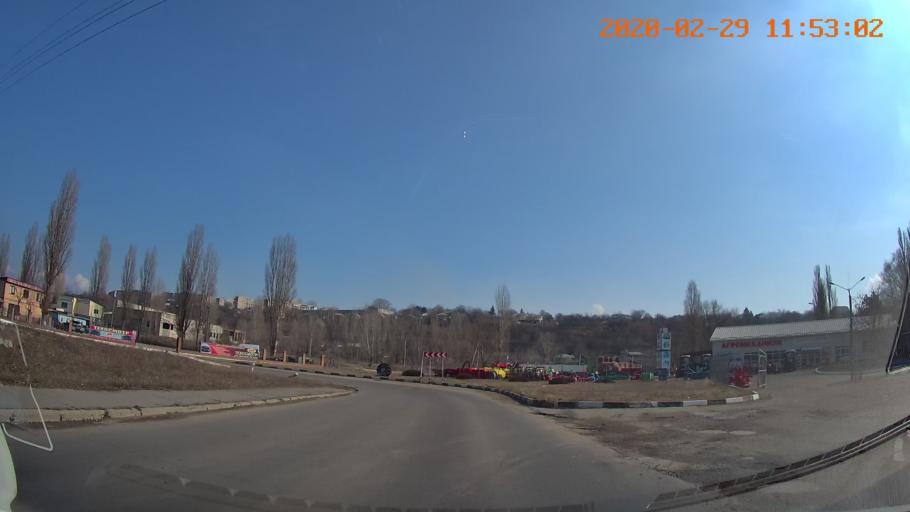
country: MD
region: Telenesti
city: Ribnita
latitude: 47.7749
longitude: 28.9896
